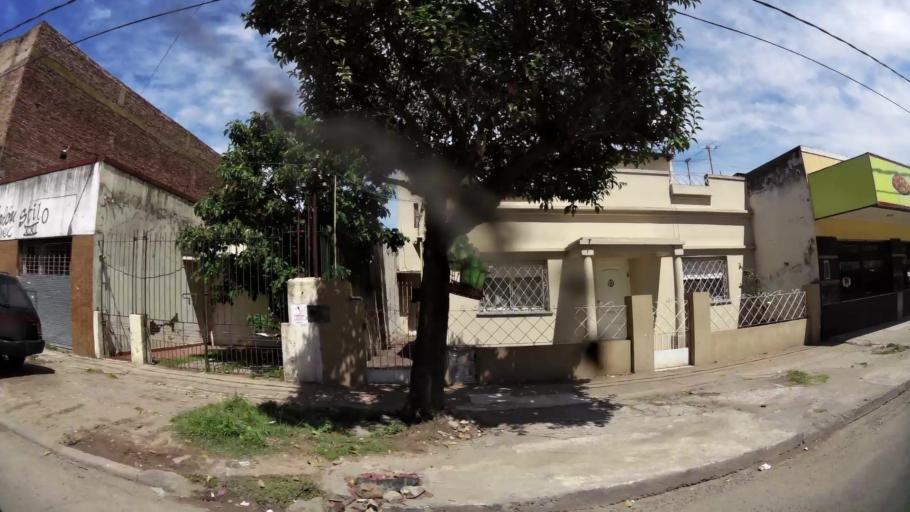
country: AR
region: Buenos Aires
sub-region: Partido de Quilmes
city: Quilmes
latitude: -34.7458
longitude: -58.2983
